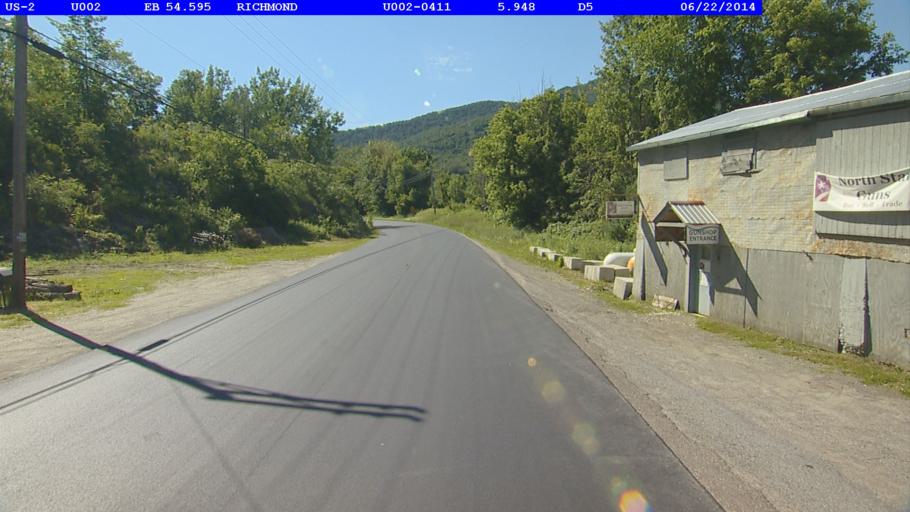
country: US
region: Vermont
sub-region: Chittenden County
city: Jericho
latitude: 44.3859
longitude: -72.9406
